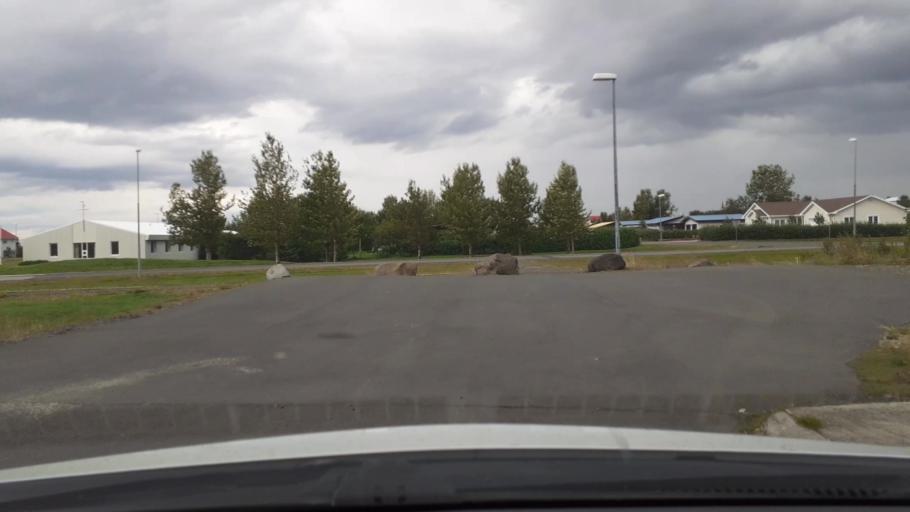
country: IS
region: West
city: Borgarnes
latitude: 64.5609
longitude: -21.7608
